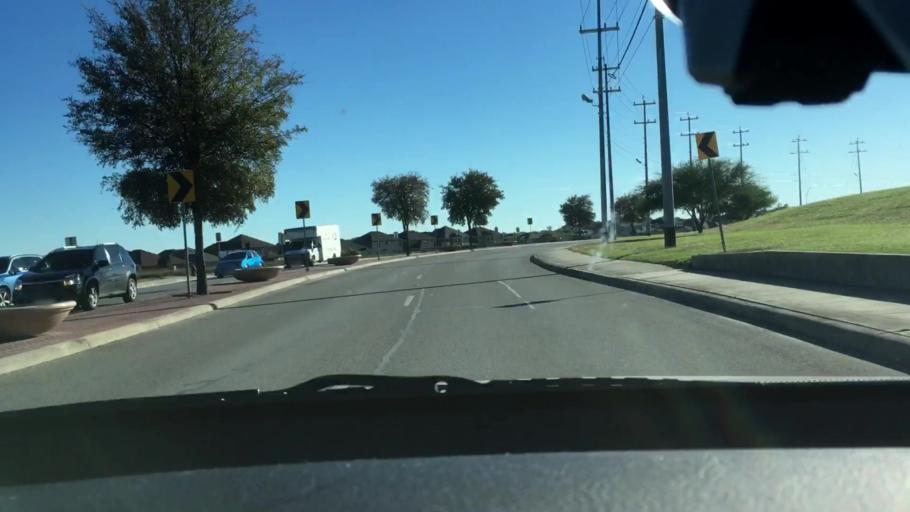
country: US
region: Texas
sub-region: Bexar County
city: Converse
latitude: 29.5424
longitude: -98.3224
